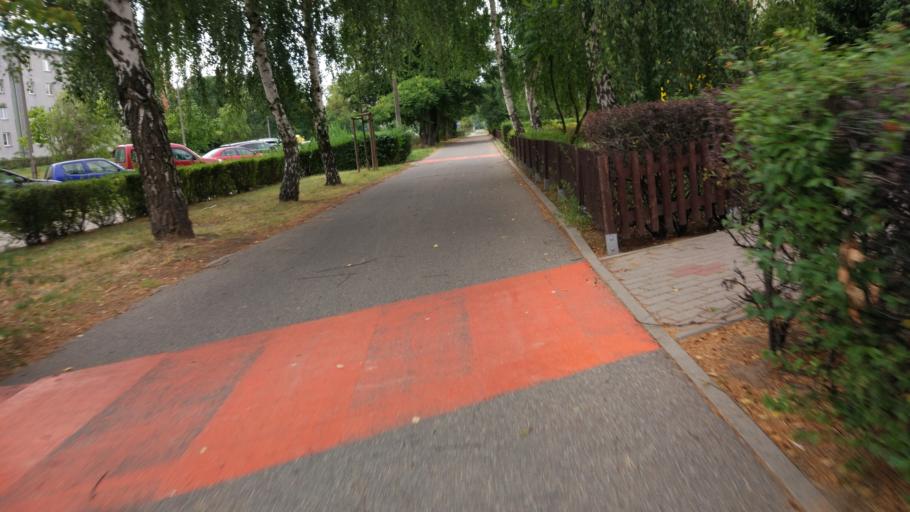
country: PL
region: Masovian Voivodeship
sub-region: Plock
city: Plock
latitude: 52.5298
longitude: 19.7557
